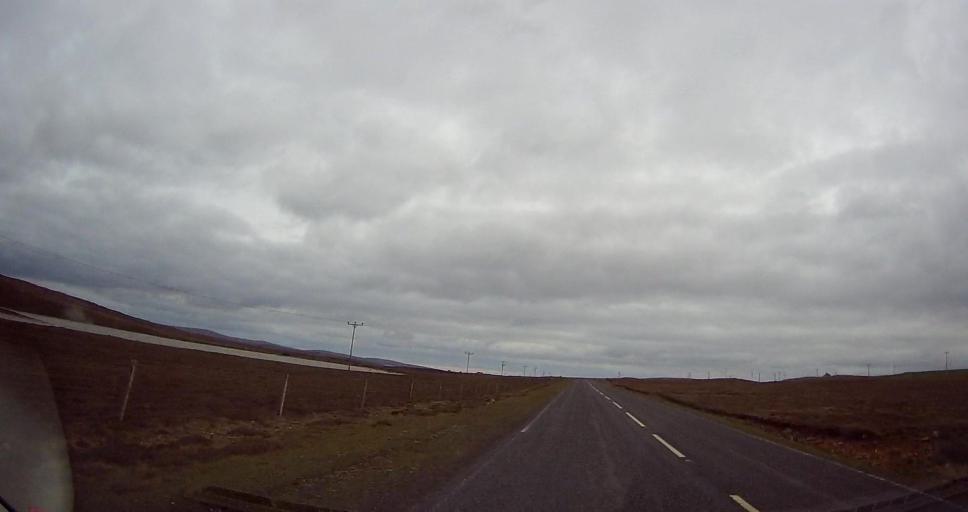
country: GB
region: Scotland
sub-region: Shetland Islands
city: Shetland
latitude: 60.7155
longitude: -0.9143
